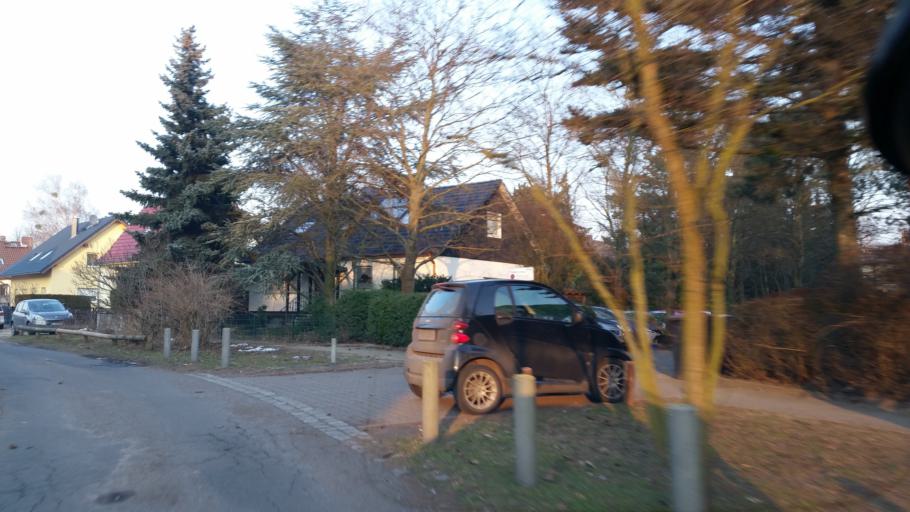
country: DE
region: Berlin
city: Lichtenrade
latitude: 52.4035
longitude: 13.4103
